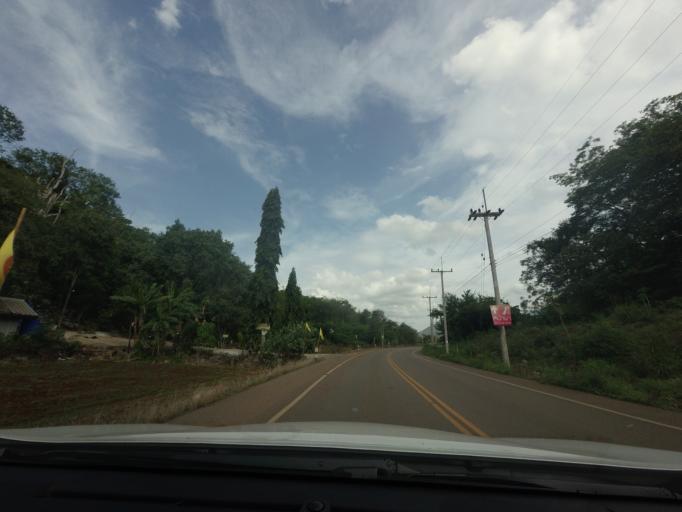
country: TH
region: Nakhon Ratchasima
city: Pak Chong
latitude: 14.5374
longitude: 101.4651
